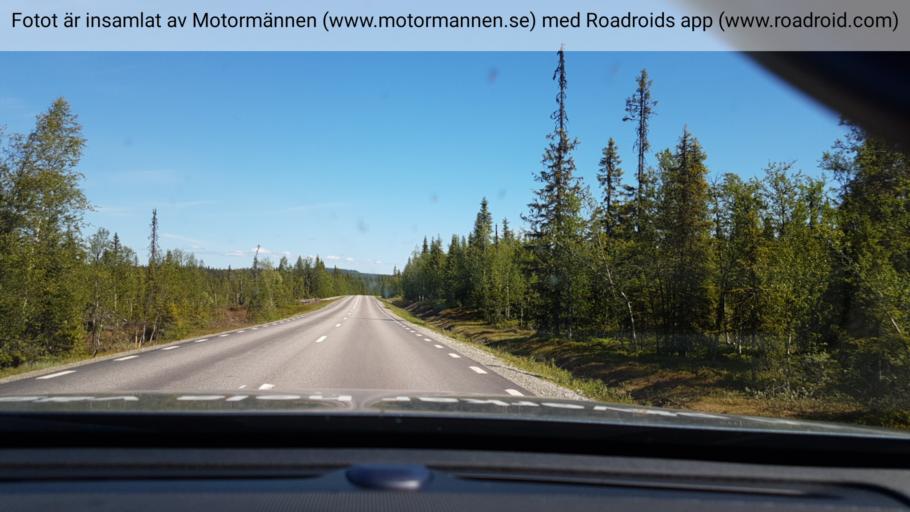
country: SE
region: Vaesterbotten
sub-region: Asele Kommun
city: Insjon
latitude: 64.7344
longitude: 17.4233
